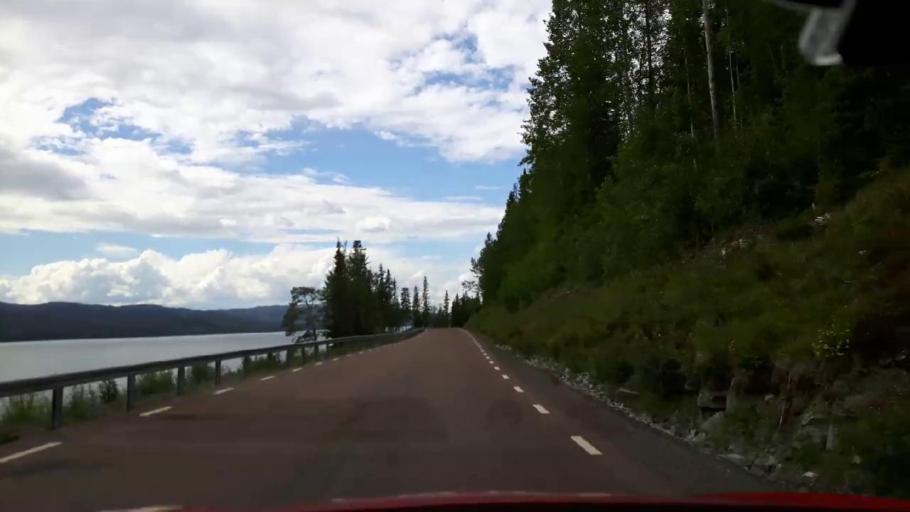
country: SE
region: Jaemtland
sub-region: Krokoms Kommun
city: Valla
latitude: 64.0863
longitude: 14.0656
